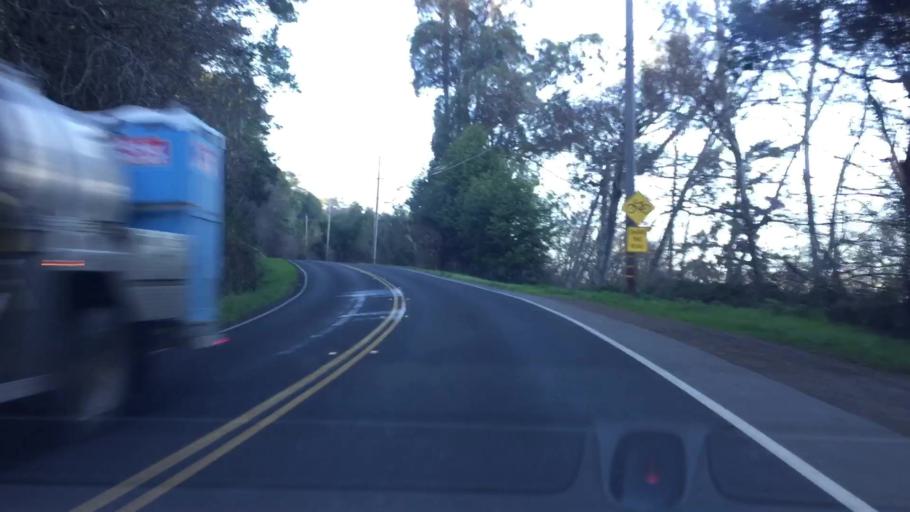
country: US
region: California
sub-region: Marin County
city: Inverness
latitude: 38.0794
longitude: -122.8331
